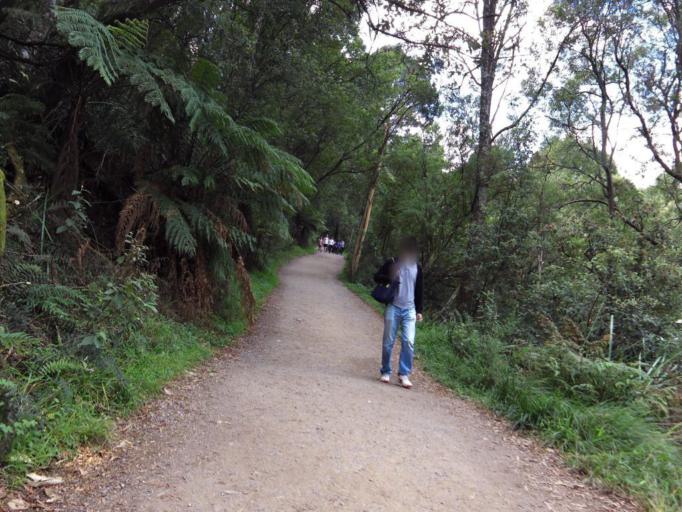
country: AU
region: Victoria
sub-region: Yarra Ranges
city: Ferny Creek
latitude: -37.8774
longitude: 145.3182
